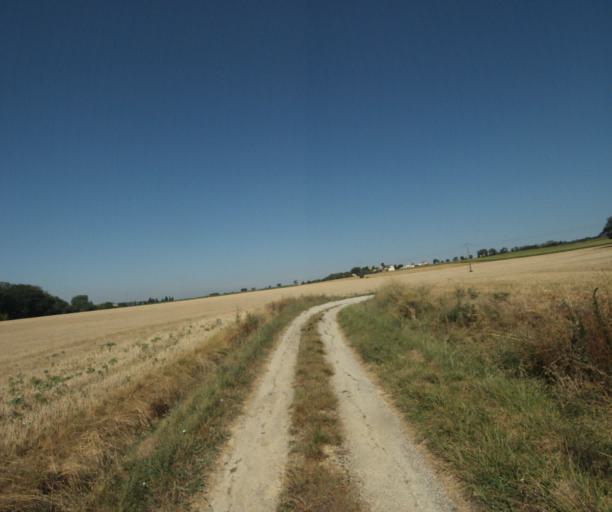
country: FR
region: Midi-Pyrenees
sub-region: Departement de la Haute-Garonne
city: Saint-Felix-Lauragais
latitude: 43.5123
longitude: 1.9183
